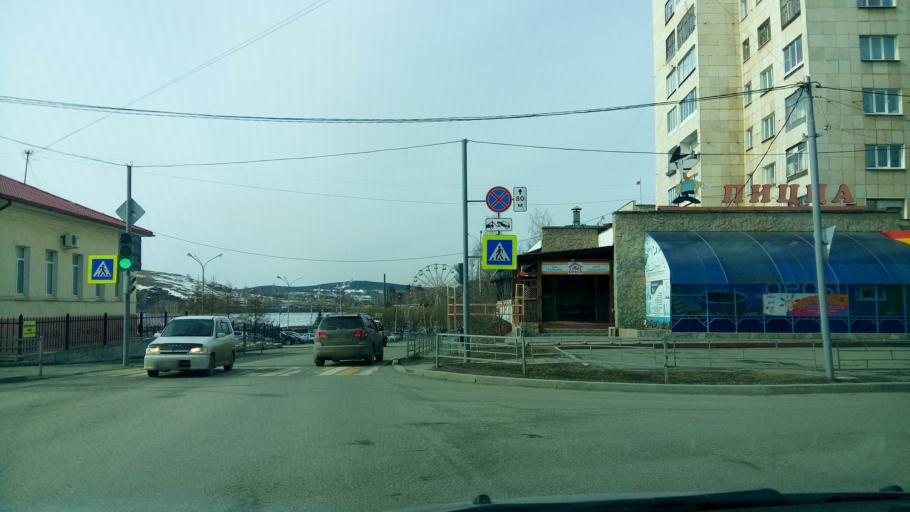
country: RU
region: Sverdlovsk
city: Nizhniy Tagil
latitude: 57.9052
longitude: 59.9639
